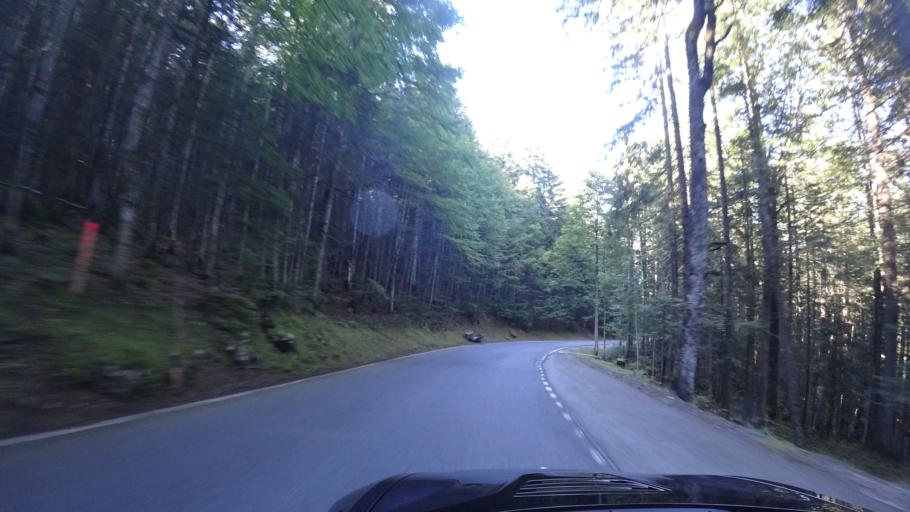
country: CH
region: Obwalden
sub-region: Obwalden
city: Lungern
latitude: 46.8275
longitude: 8.1245
